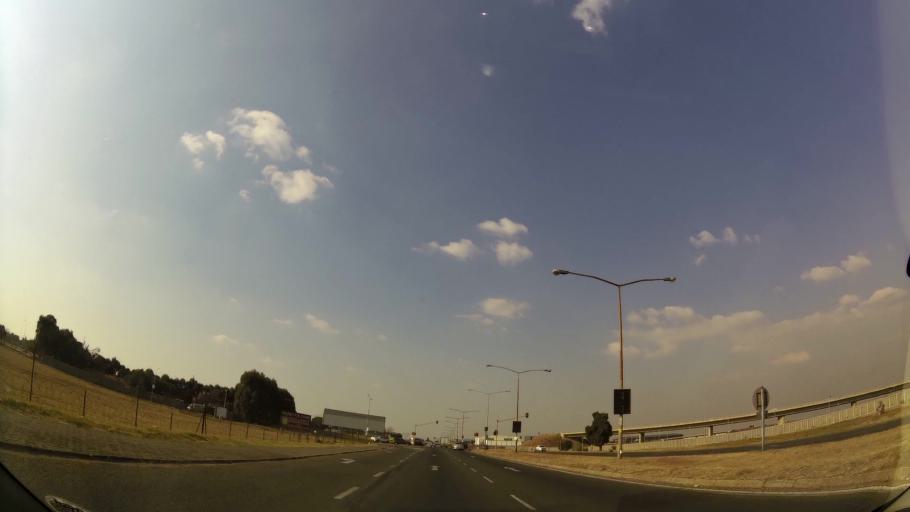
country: ZA
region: Gauteng
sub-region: City of Johannesburg Metropolitan Municipality
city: Modderfontein
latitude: -26.1018
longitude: 28.2484
